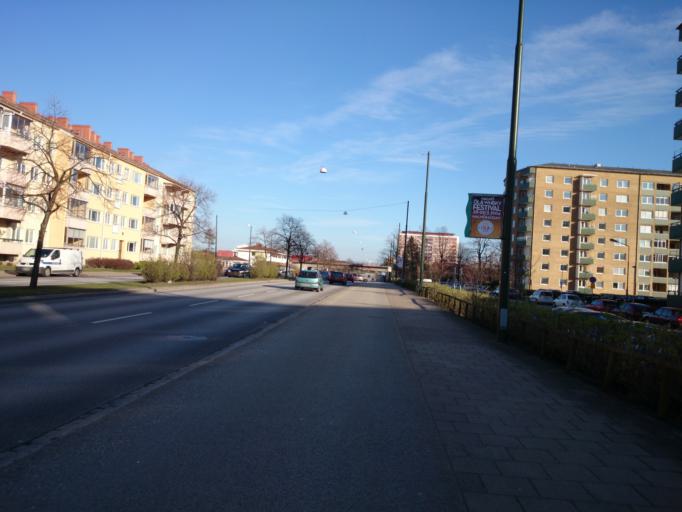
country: SE
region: Skane
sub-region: Malmo
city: Malmoe
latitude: 55.6021
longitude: 13.0340
